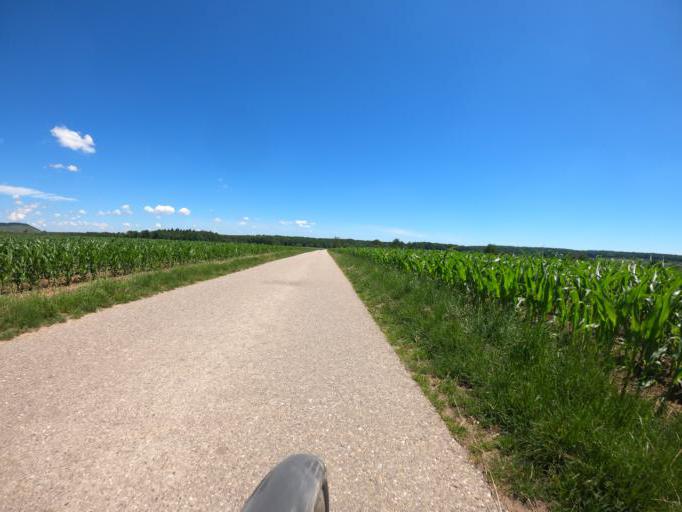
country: DE
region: Baden-Wuerttemberg
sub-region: Regierungsbezirk Stuttgart
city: Sersheim
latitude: 48.9709
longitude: 9.0145
